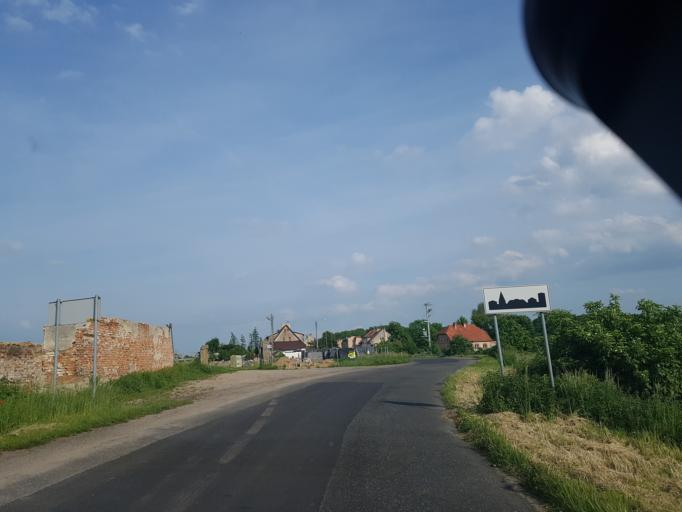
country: PL
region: Lower Silesian Voivodeship
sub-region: Powiat wroclawski
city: Zorawina
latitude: 50.9085
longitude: 17.0861
